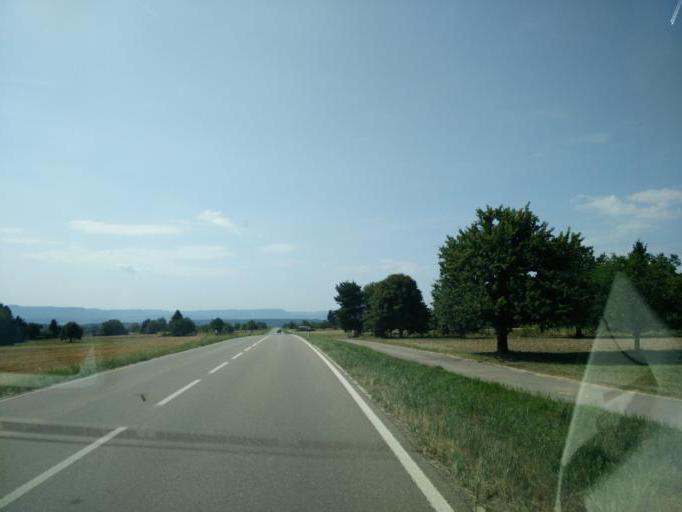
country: DE
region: Baden-Wuerttemberg
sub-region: Tuebingen Region
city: Kusterdingen
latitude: 48.5516
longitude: 9.0951
